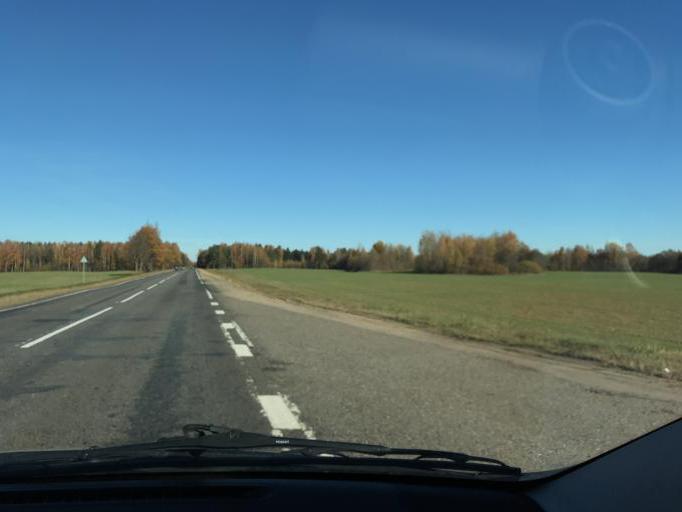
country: BY
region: Vitebsk
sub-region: Ushatski Rayon
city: Ushachy
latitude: 55.0870
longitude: 28.7561
